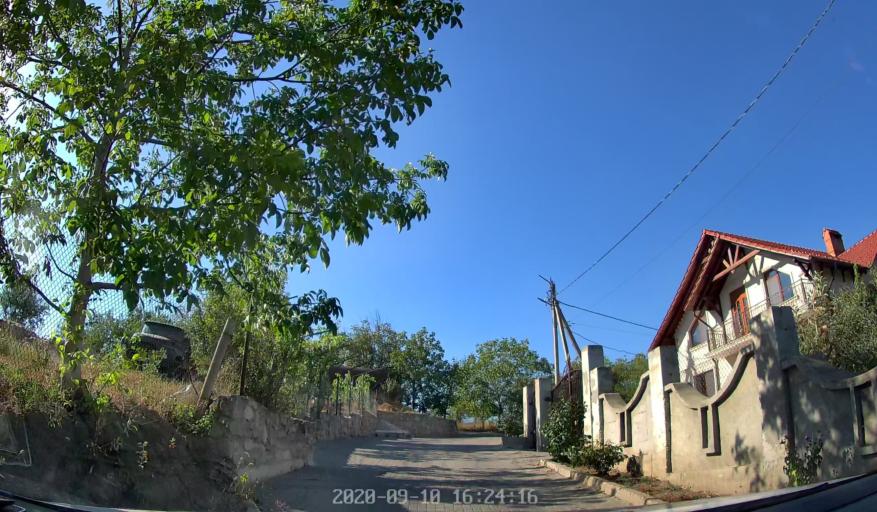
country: MD
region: Chisinau
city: Stauceni
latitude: 47.0533
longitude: 28.9210
